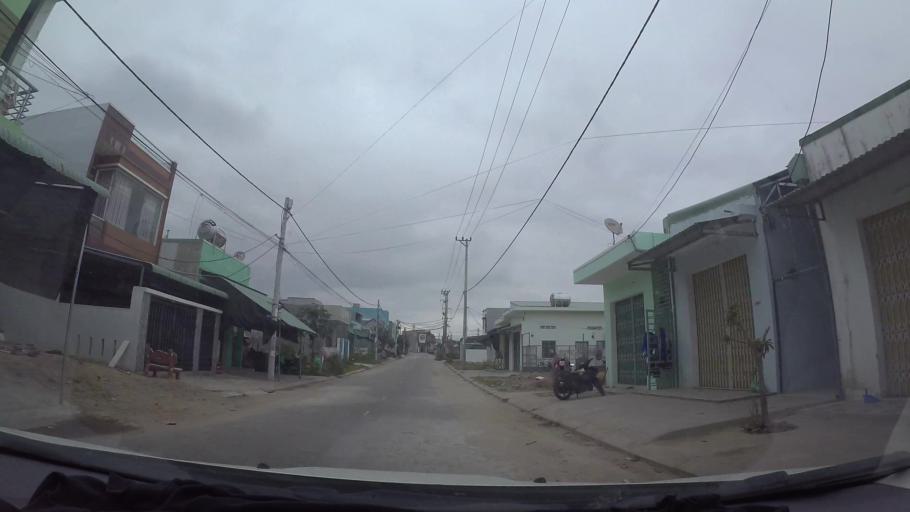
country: VN
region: Da Nang
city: Lien Chieu
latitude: 16.0695
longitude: 108.1407
